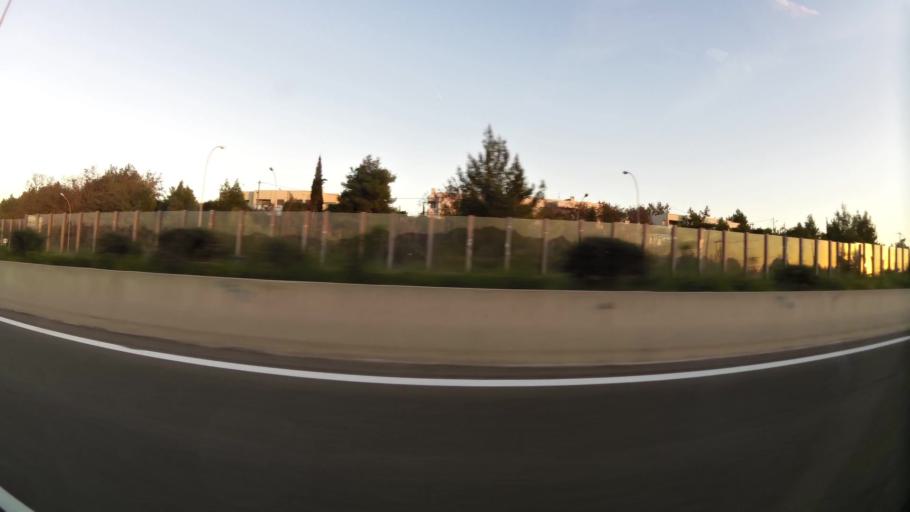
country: GR
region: Attica
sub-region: Nomarchia Athinas
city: Ekali
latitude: 38.1194
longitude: 23.8312
